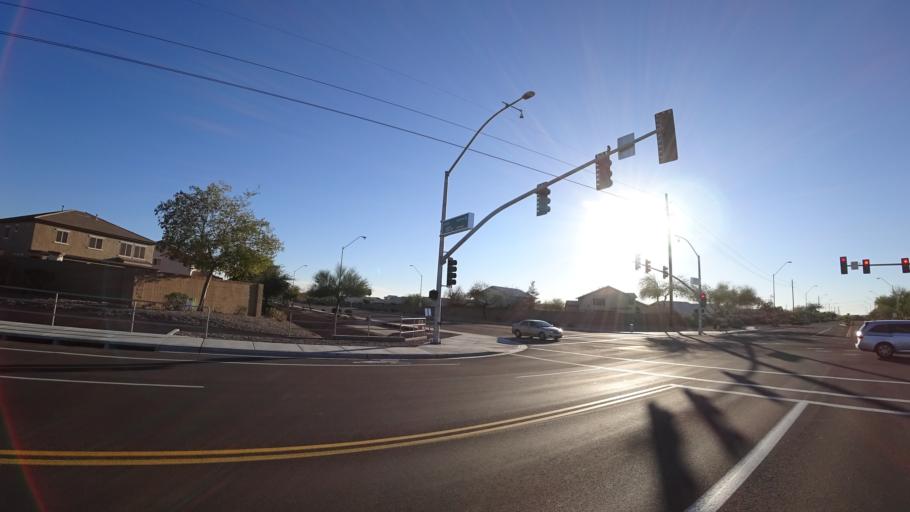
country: US
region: Arizona
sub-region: Maricopa County
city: Sun City West
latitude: 33.6818
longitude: -112.2895
